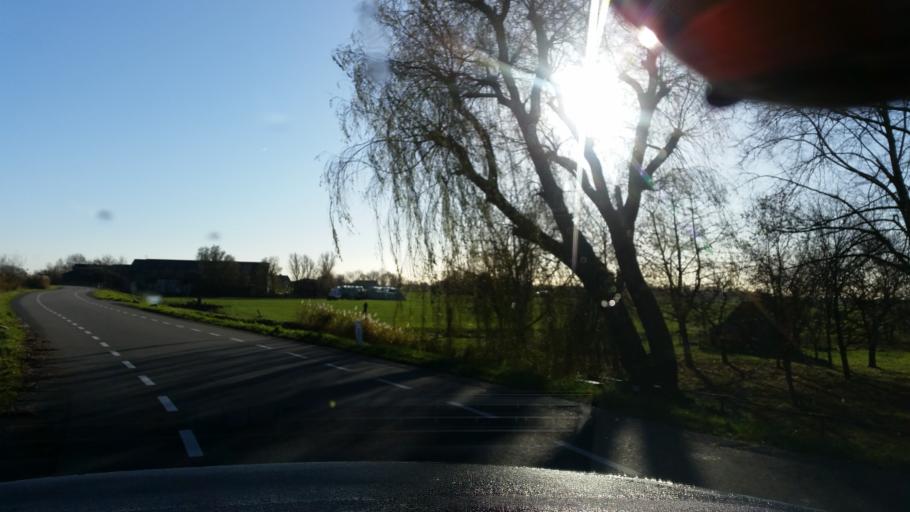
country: NL
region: North Holland
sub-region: Gemeente Ouder-Amstel
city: Ouderkerk aan de Amstel
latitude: 52.2863
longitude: 4.9165
